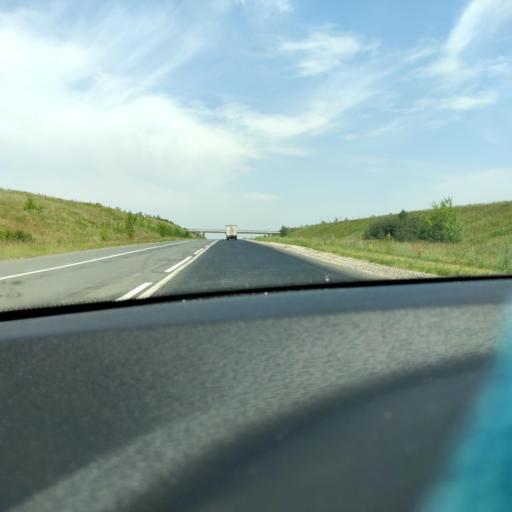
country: RU
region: Samara
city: Petra-Dubrava
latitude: 53.2978
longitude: 50.4021
